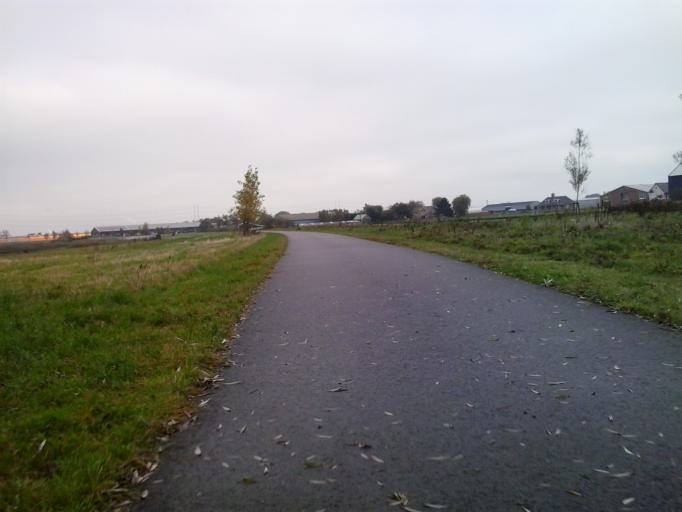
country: NL
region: South Holland
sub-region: Gemeente Lansingerland
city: Berkel en Rodenrijs
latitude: 52.0094
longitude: 4.4661
